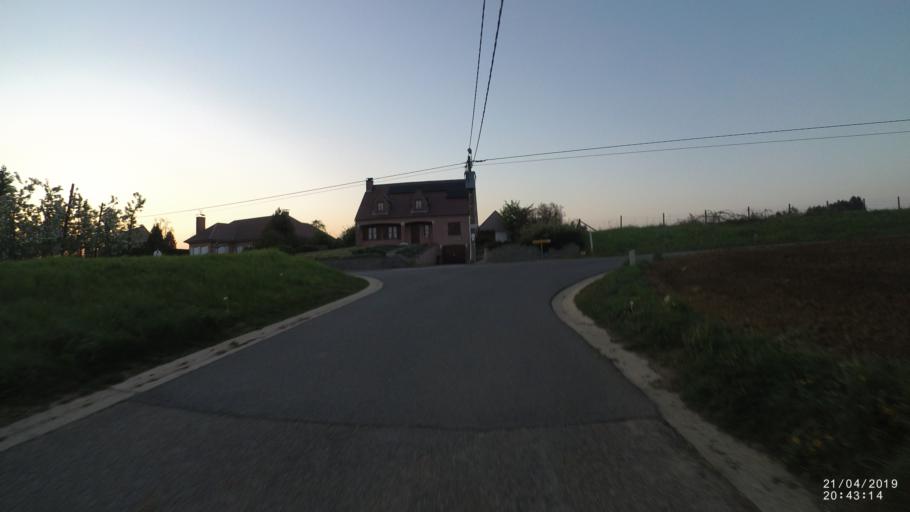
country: BE
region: Flanders
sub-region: Provincie Vlaams-Brabant
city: Lubbeek
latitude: 50.9070
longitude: 4.8571
